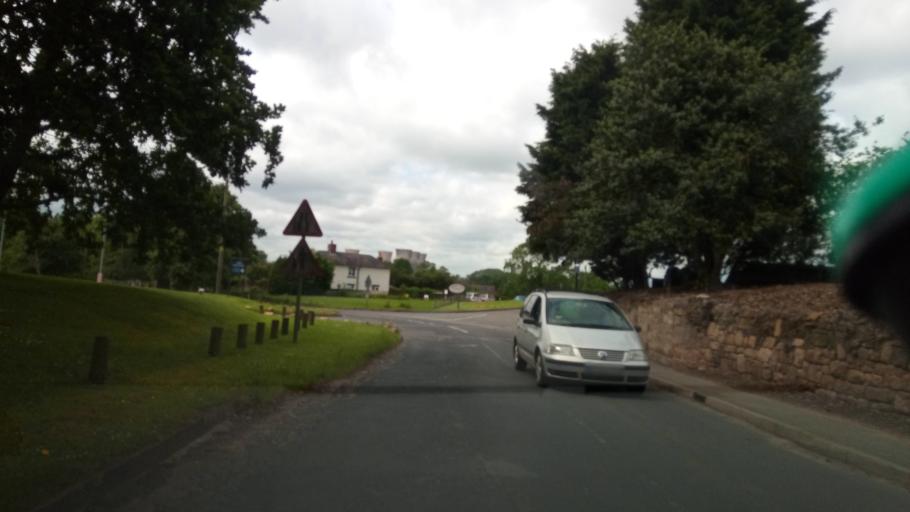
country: GB
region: England
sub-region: Derbyshire
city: Findern
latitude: 52.8669
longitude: -1.5166
